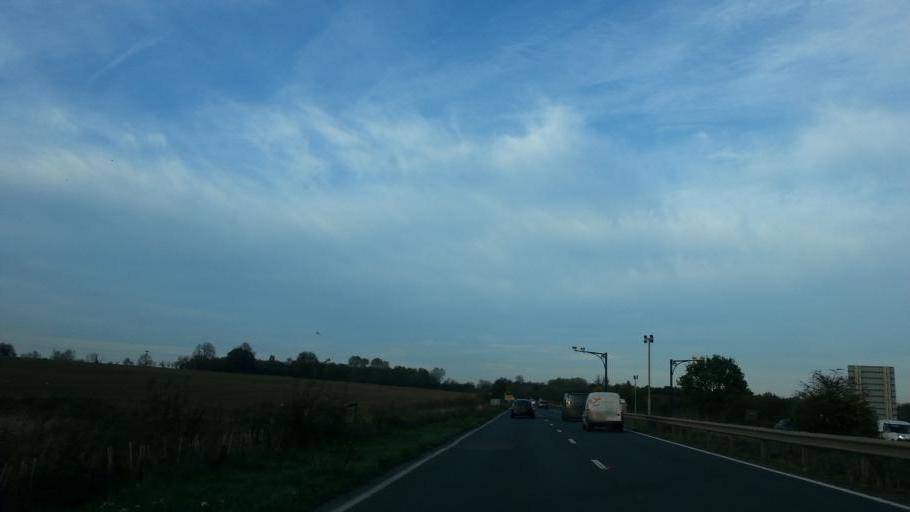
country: GB
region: England
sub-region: Cambridgeshire
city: Little Paxton
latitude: 52.2710
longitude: -0.2612
